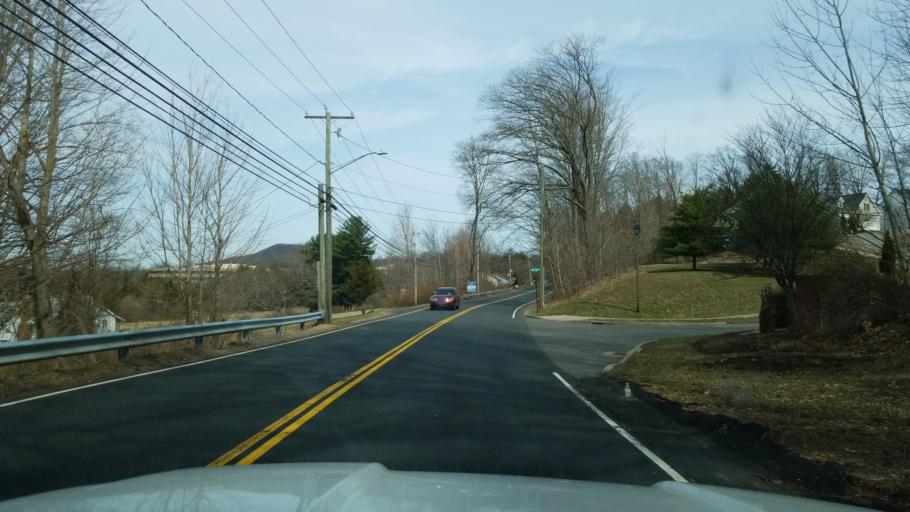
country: US
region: Connecticut
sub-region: New Haven County
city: Meriden
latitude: 41.5374
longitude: -72.7521
